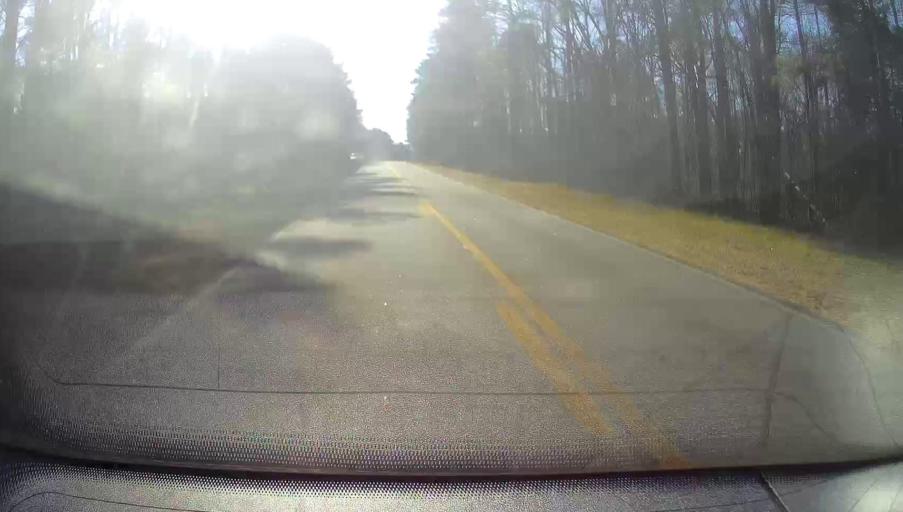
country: US
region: Georgia
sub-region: Monroe County
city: Forsyth
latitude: 33.0821
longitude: -83.8473
